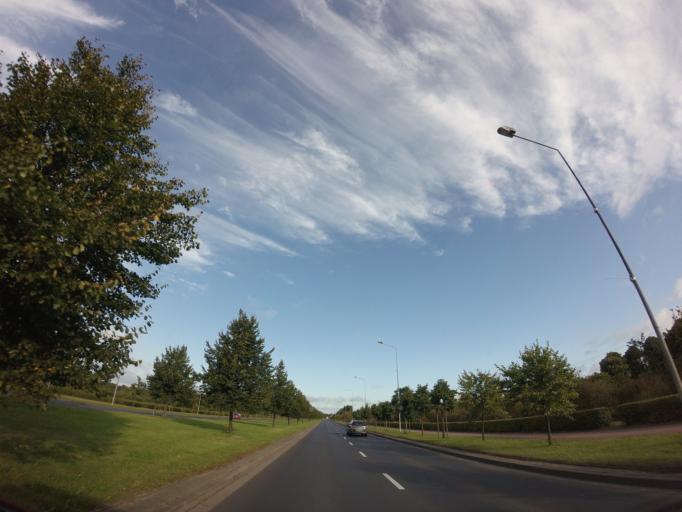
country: PL
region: West Pomeranian Voivodeship
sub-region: Szczecin
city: Szczecin
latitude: 53.4299
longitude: 14.4987
